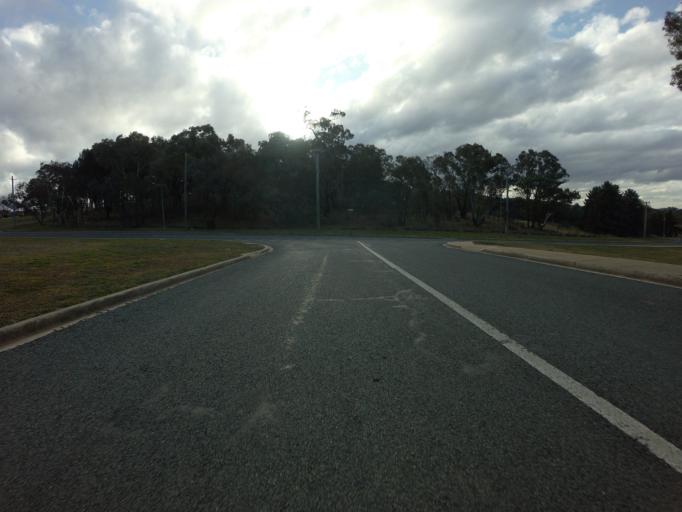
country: AU
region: Australian Capital Territory
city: Forrest
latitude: -35.3040
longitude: 149.1139
